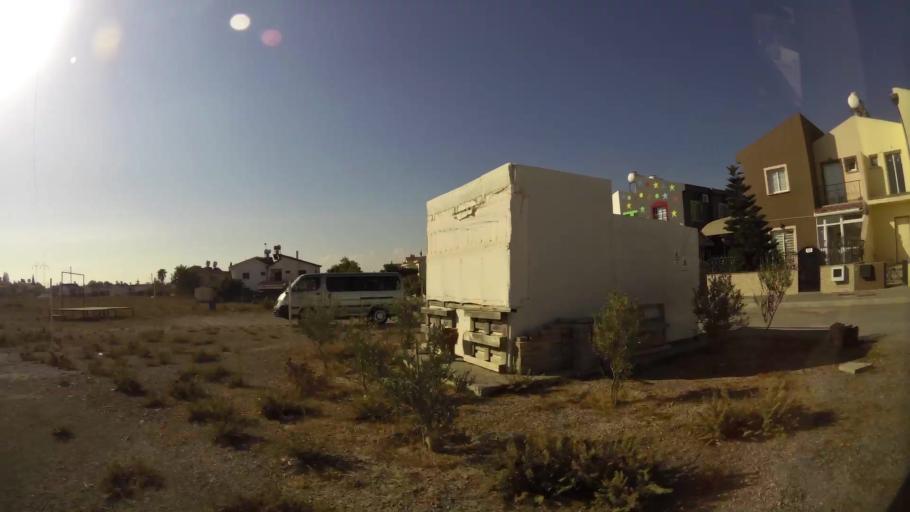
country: CY
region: Lefkosia
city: Nicosia
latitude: 35.2156
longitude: 33.3677
